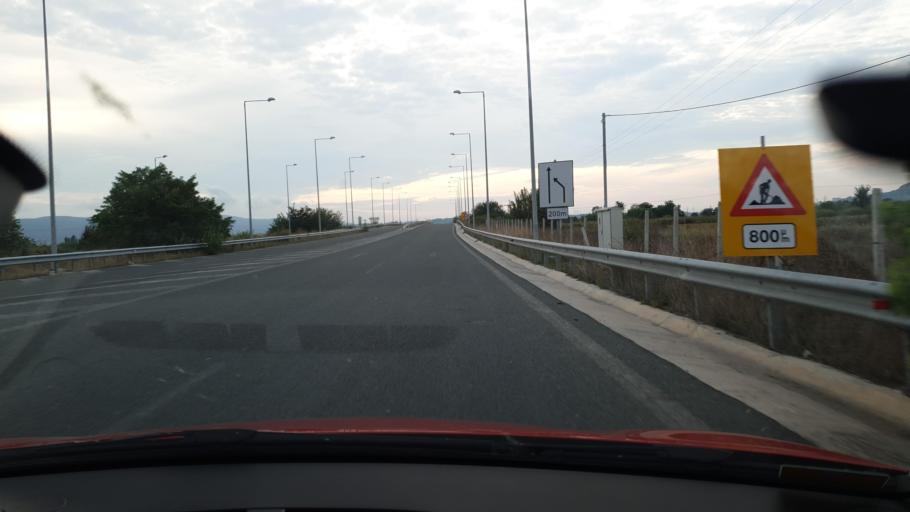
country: GR
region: Central Macedonia
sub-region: Nomos Thessalonikis
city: Assiros
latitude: 40.7831
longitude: 23.0227
